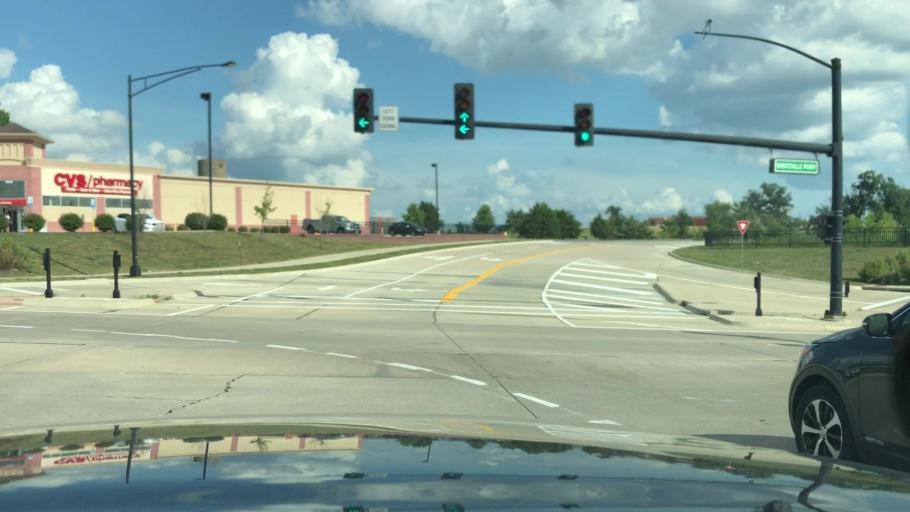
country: US
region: Missouri
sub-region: Saint Charles County
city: Wentzville
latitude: 38.8243
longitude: -90.8772
